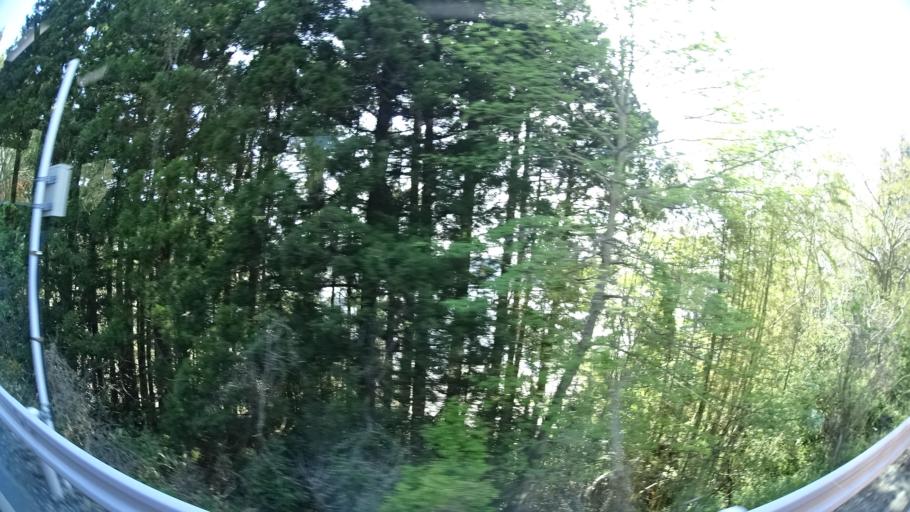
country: JP
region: Iwate
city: Ofunato
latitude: 38.9957
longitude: 141.7102
